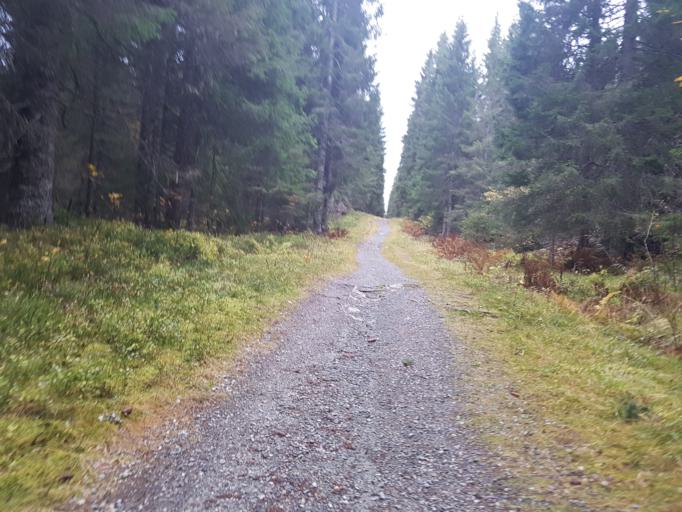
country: NO
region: Sor-Trondelag
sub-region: Melhus
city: Melhus
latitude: 63.3815
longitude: 10.2535
